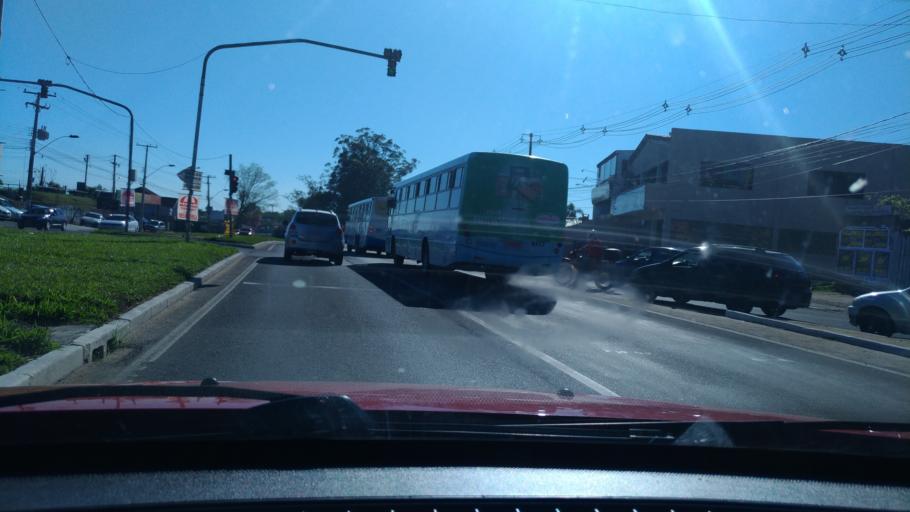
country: BR
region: Rio Grande do Sul
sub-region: Viamao
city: Viamao
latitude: -30.0947
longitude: -51.0794
